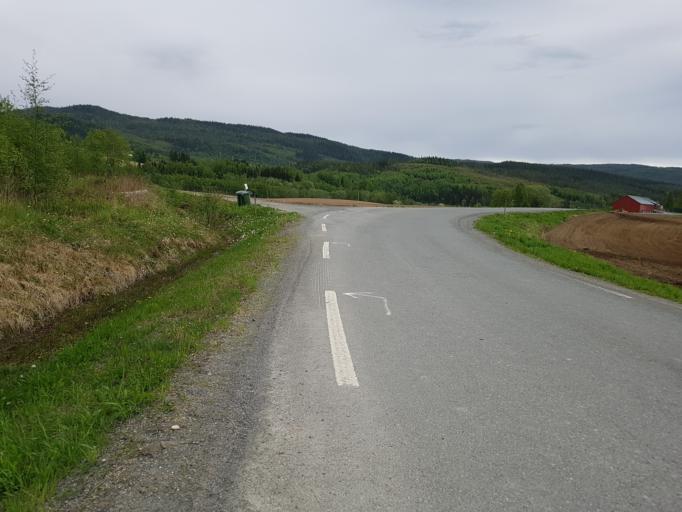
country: NO
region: Nord-Trondelag
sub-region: Levanger
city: Skogn
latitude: 63.6213
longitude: 11.2808
